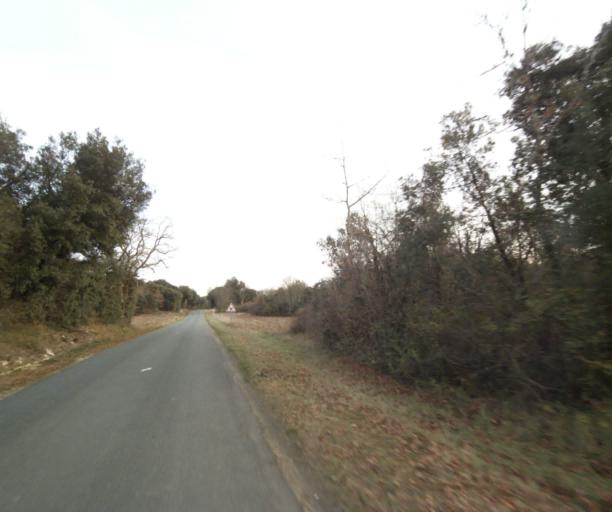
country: FR
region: Poitou-Charentes
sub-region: Departement de la Charente-Maritime
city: Bussac-sur-Charente
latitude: 45.8136
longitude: -0.5969
